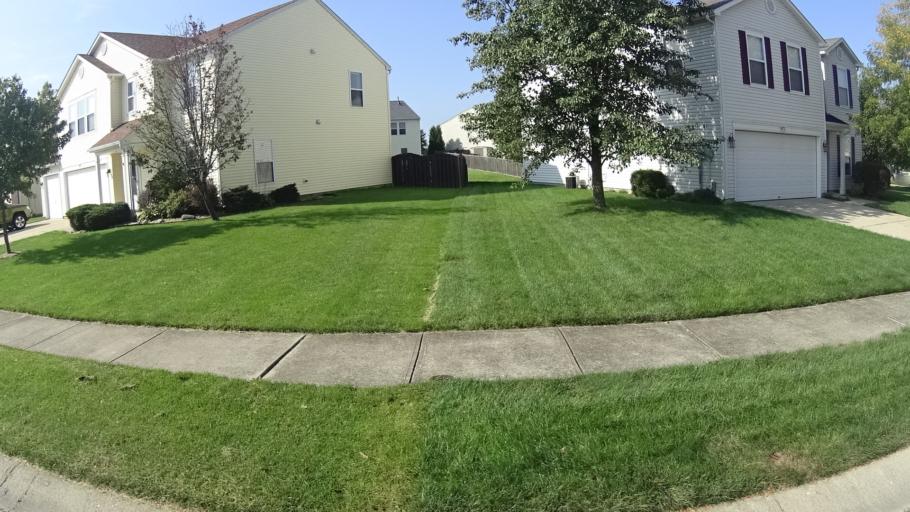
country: US
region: Indiana
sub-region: Madison County
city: Ingalls
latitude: 39.9869
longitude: -85.8461
